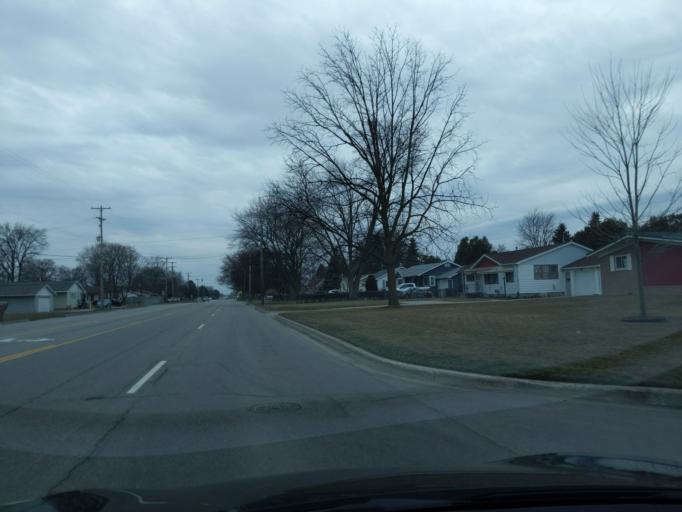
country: US
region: Michigan
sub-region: Bay County
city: Bay City
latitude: 43.6239
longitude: -83.9199
